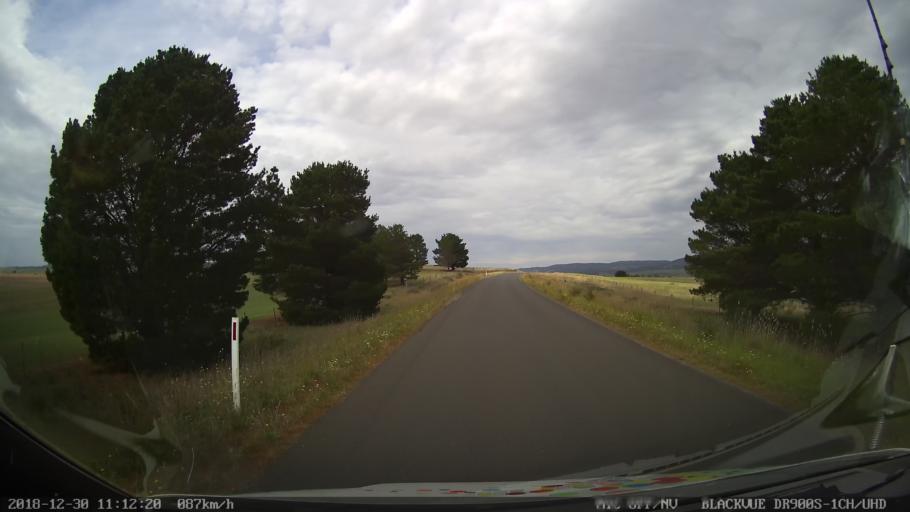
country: AU
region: New South Wales
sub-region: Snowy River
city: Jindabyne
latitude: -36.5275
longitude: 148.7579
